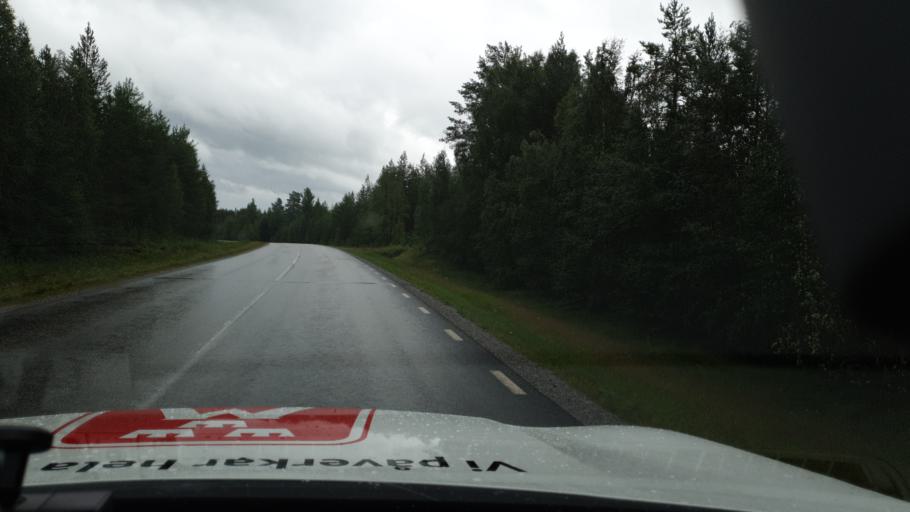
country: SE
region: Norrbotten
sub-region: Pitea Kommun
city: Roknas
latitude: 65.3404
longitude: 21.1508
